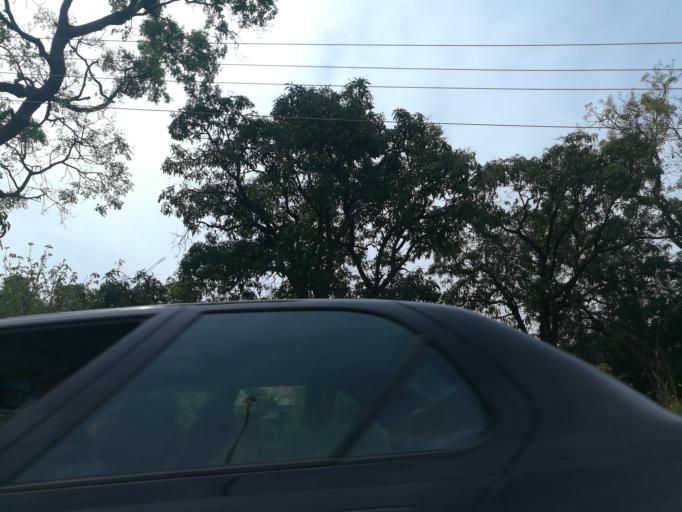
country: NG
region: Plateau
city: Jos
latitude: 9.9103
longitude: 8.8837
